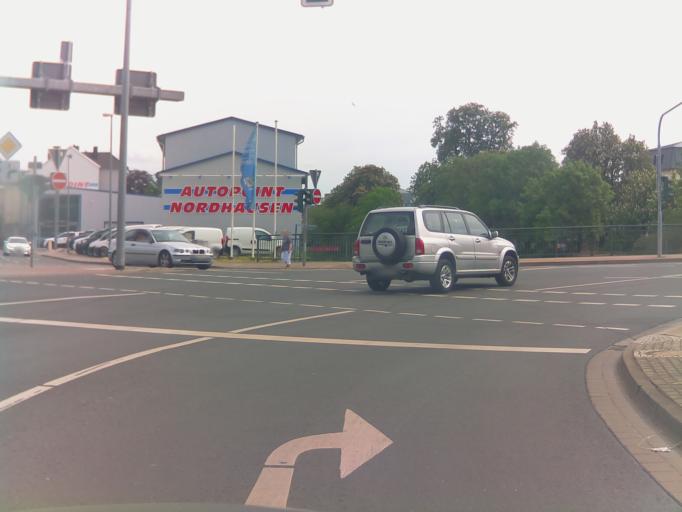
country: DE
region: Thuringia
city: Nordhausen
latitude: 51.4985
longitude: 10.7889
